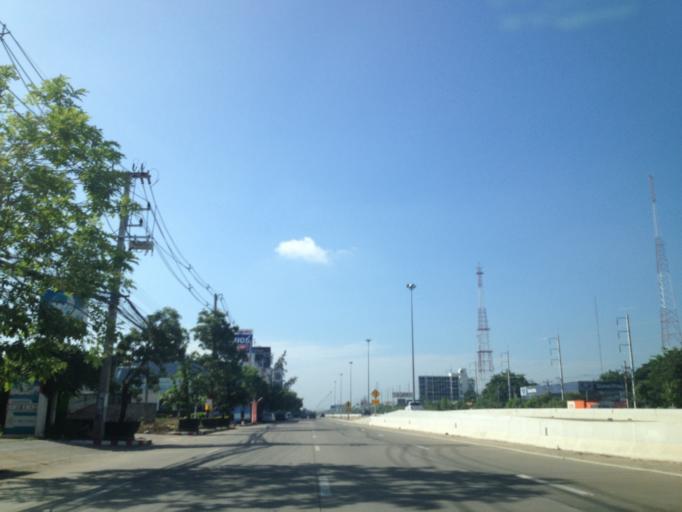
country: TH
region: Chiang Mai
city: Chiang Mai
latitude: 18.7817
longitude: 99.0273
